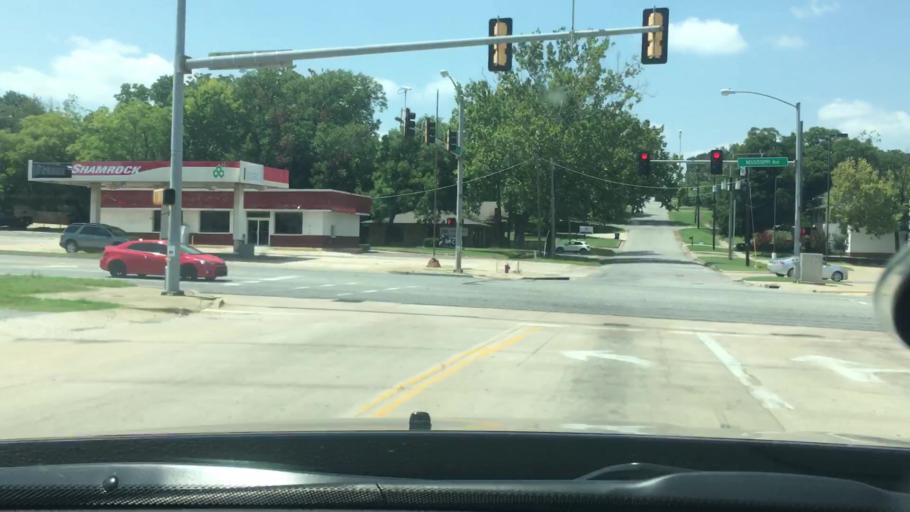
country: US
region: Oklahoma
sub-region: Atoka County
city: Atoka
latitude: 34.3860
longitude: -96.1278
